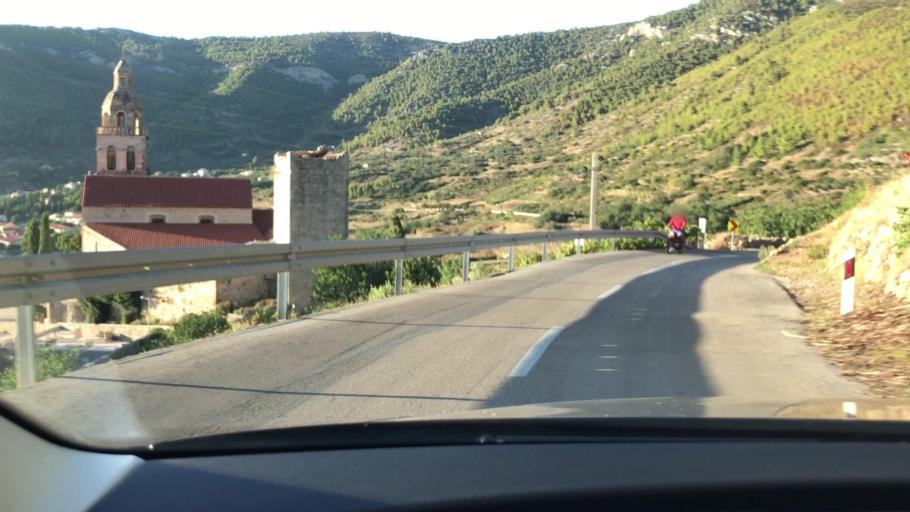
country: HR
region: Splitsko-Dalmatinska
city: Komiza
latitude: 43.0401
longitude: 16.0966
